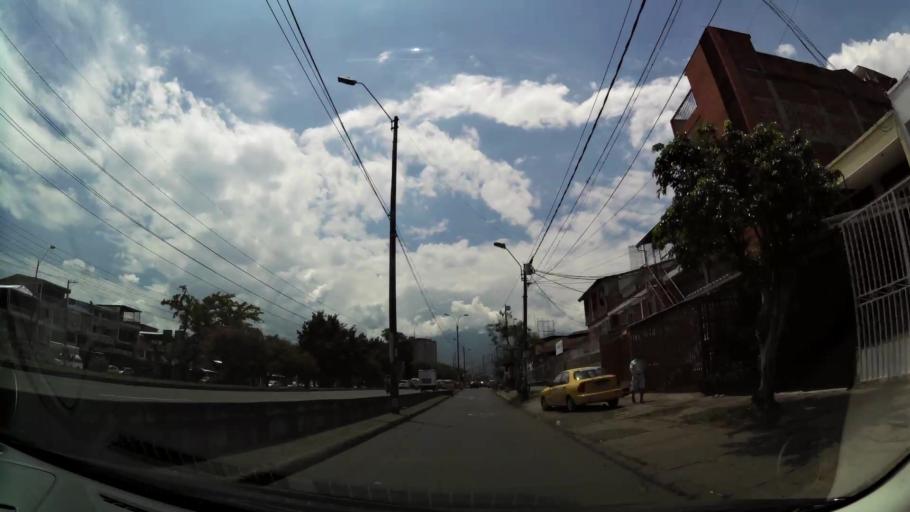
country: CO
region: Valle del Cauca
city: Cali
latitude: 3.4371
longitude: -76.5119
